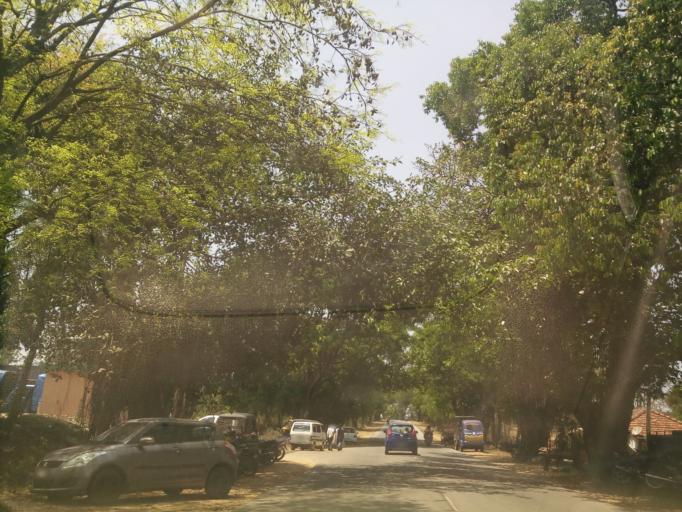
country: IN
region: Karnataka
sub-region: Hassan
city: Alur
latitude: 12.9482
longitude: 75.9601
